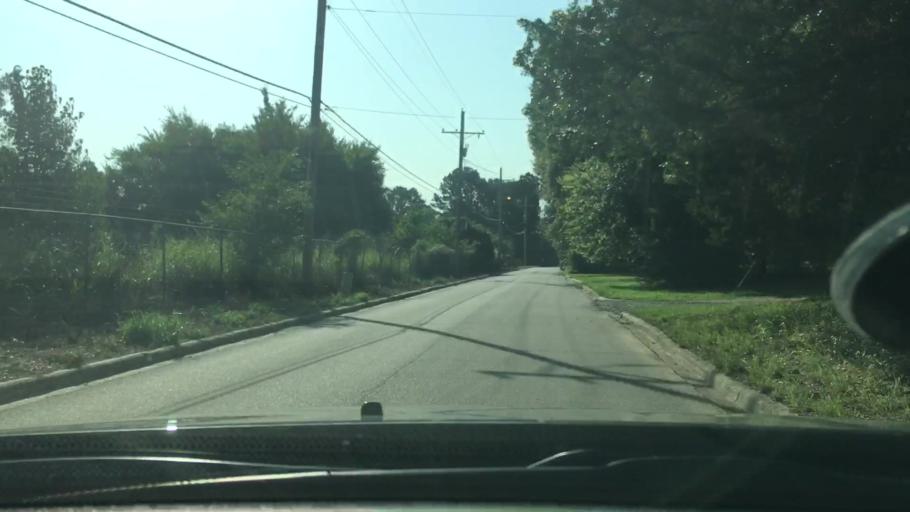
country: US
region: Oklahoma
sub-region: Atoka County
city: Atoka
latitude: 34.3927
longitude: -96.1373
